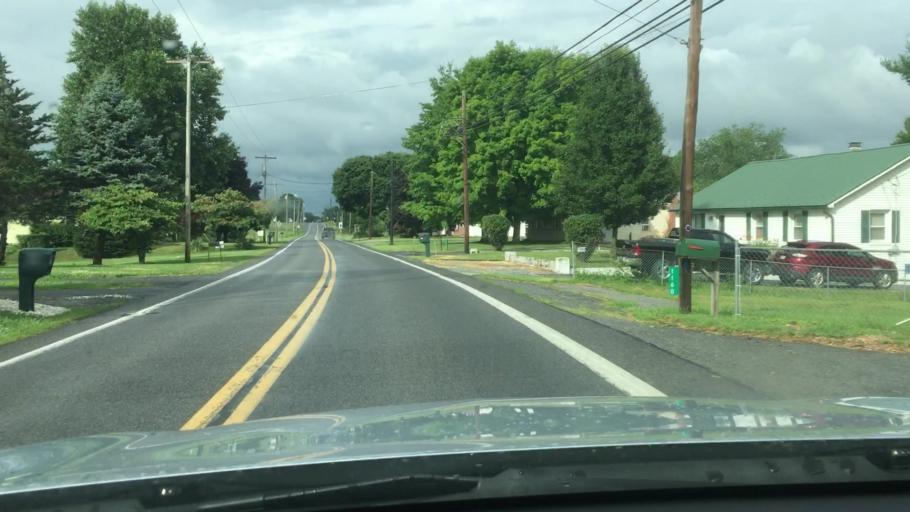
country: US
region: Pennsylvania
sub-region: Franklin County
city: Chambersburg
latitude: 39.9075
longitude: -77.7118
